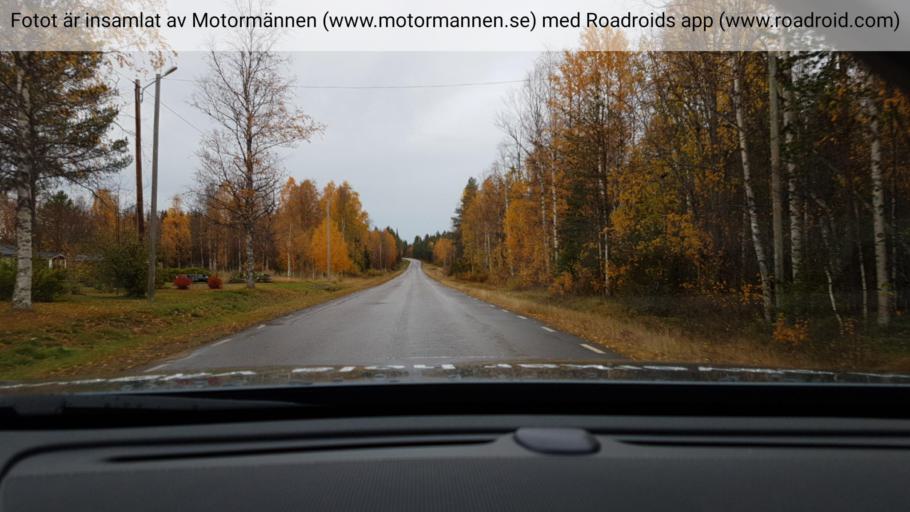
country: SE
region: Norrbotten
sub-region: Pajala Kommun
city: Pajala
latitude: 67.1592
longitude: 22.6565
